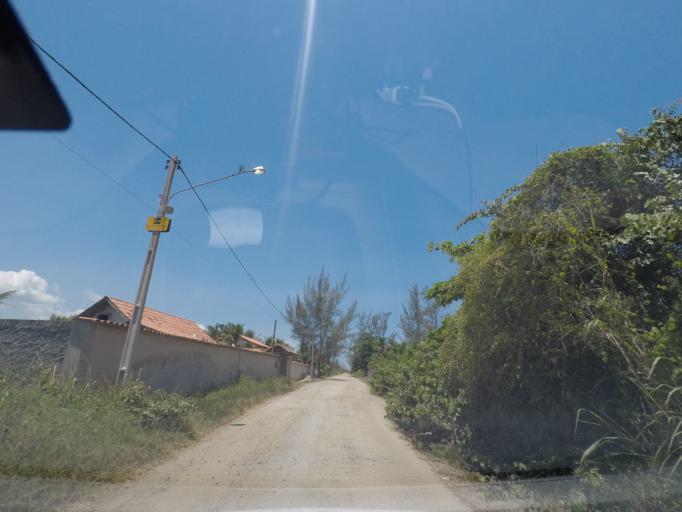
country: BR
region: Rio de Janeiro
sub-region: Niteroi
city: Niteroi
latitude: -22.9682
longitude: -42.9859
